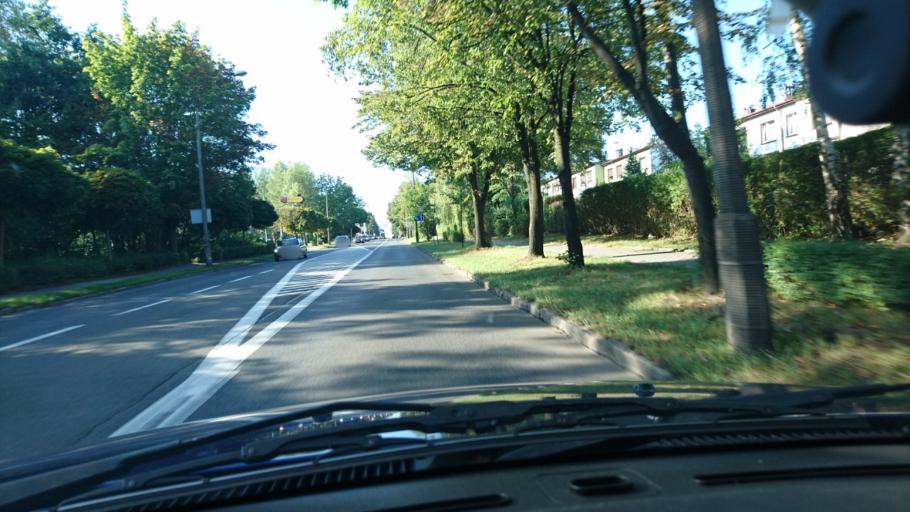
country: PL
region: Silesian Voivodeship
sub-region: Gliwice
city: Gliwice
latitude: 50.3223
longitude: 18.6630
